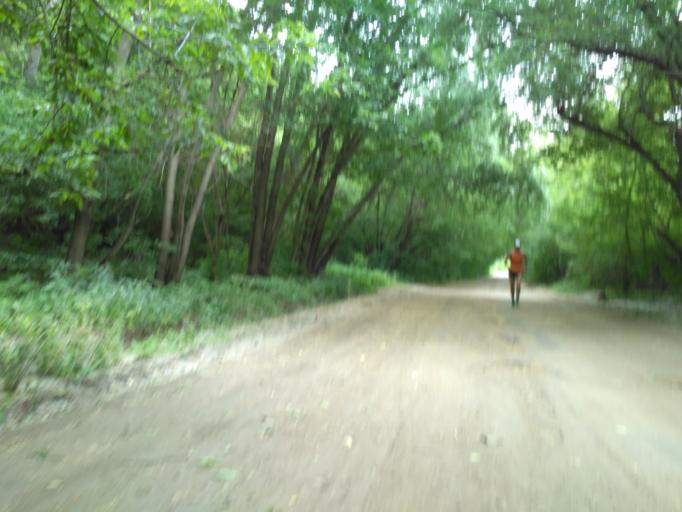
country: RU
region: Nizjnij Novgorod
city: Nizhniy Novgorod
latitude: 56.2900
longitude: 43.9686
